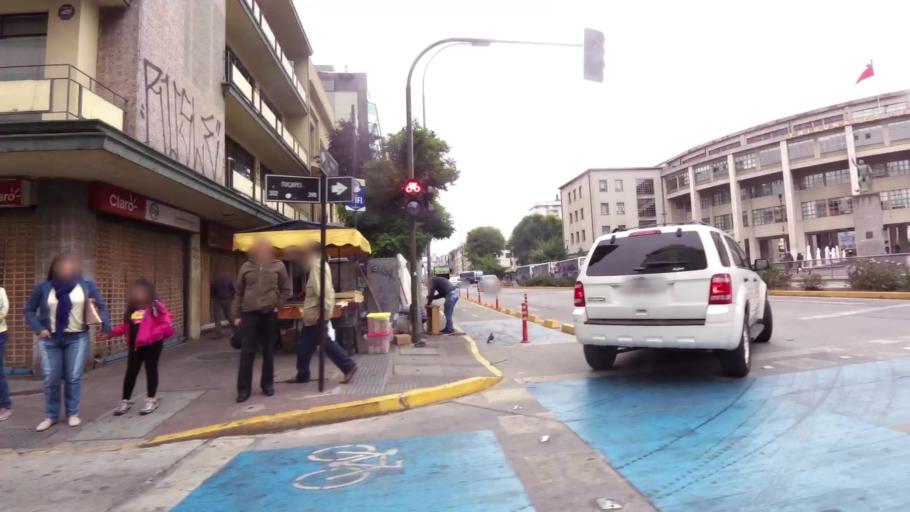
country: CL
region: Biobio
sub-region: Provincia de Concepcion
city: Concepcion
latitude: -36.8254
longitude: -73.0444
